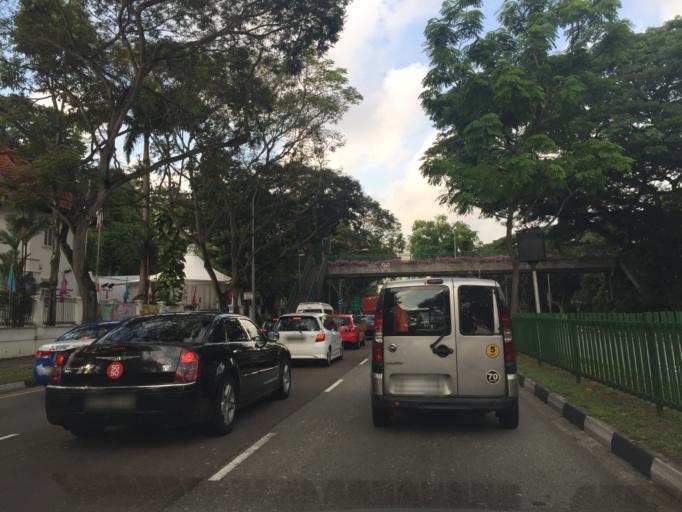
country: SG
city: Singapore
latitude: 1.3238
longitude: 103.8267
